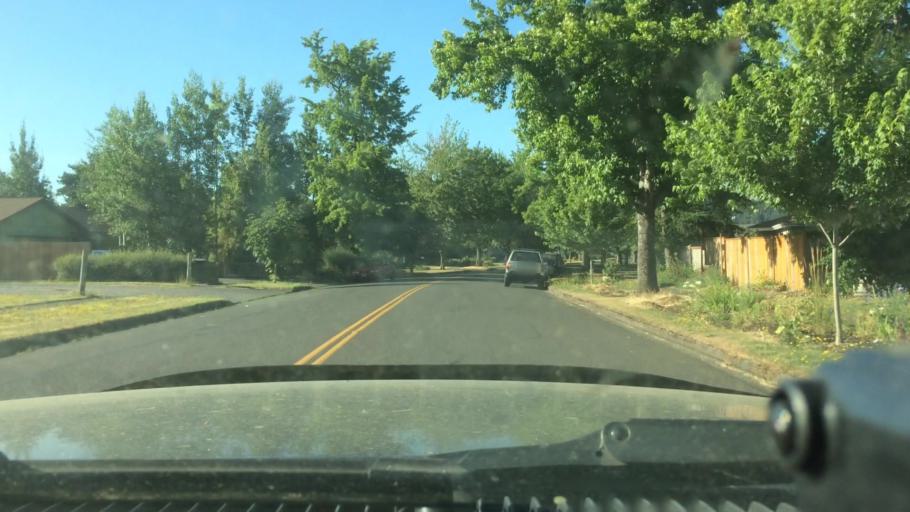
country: US
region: Oregon
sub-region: Lane County
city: Eugene
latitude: 44.0396
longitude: -123.1125
